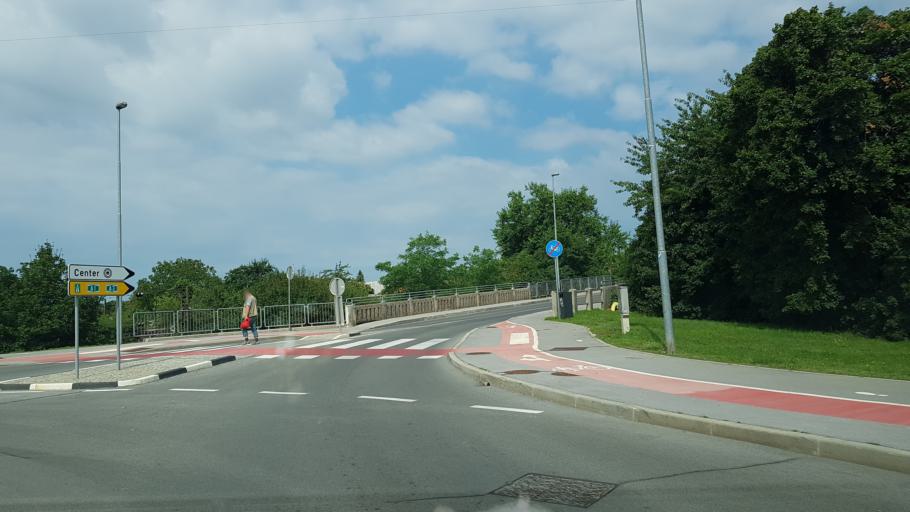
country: SI
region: Sezana
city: Sezana
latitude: 45.7056
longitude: 13.8735
